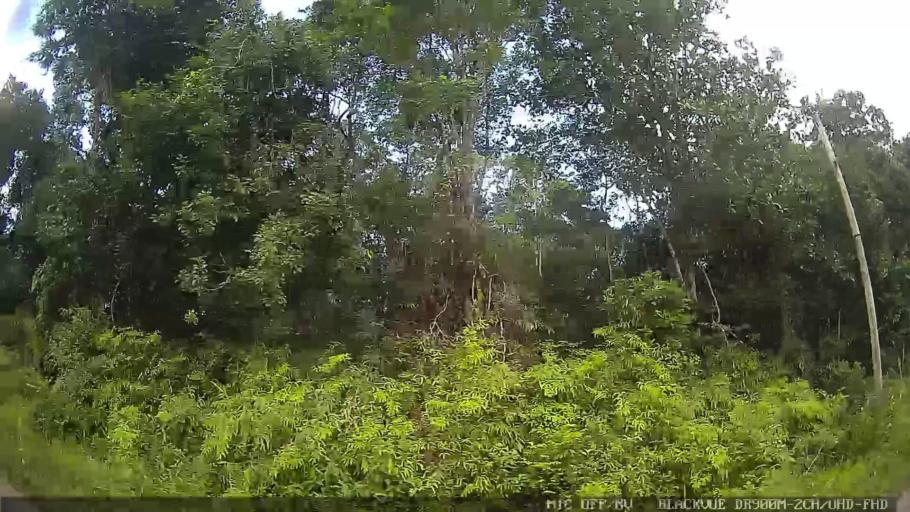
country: BR
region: Sao Paulo
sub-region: Itanhaem
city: Itanhaem
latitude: -24.1782
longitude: -46.9362
